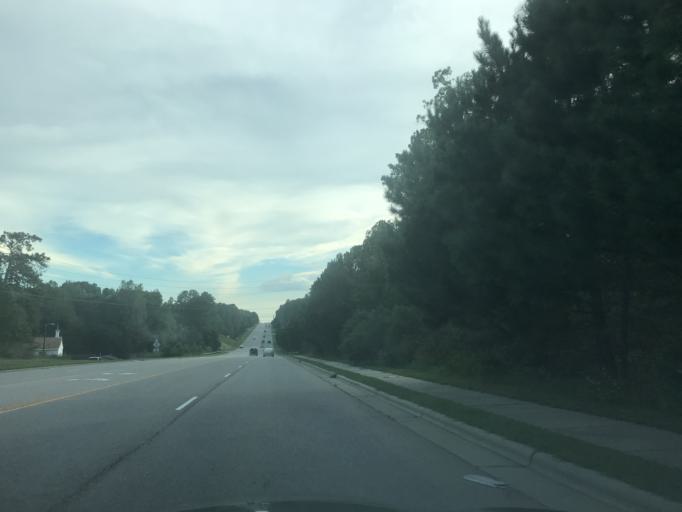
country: US
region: North Carolina
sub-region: Wake County
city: Green Level
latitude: 35.7724
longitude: -78.8736
